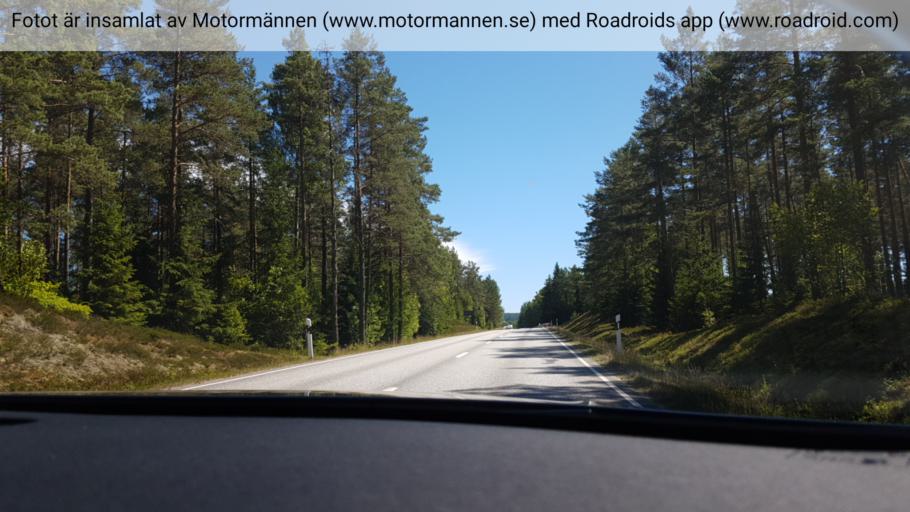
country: SE
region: Joenkoeping
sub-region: Gnosjo Kommun
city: Gnosjoe
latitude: 57.3676
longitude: 13.7443
